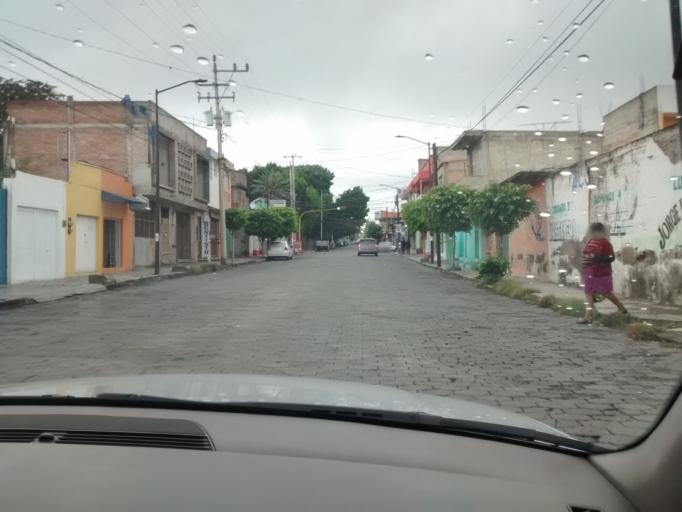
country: MX
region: Puebla
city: Tehuacan
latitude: 18.4568
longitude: -97.3959
